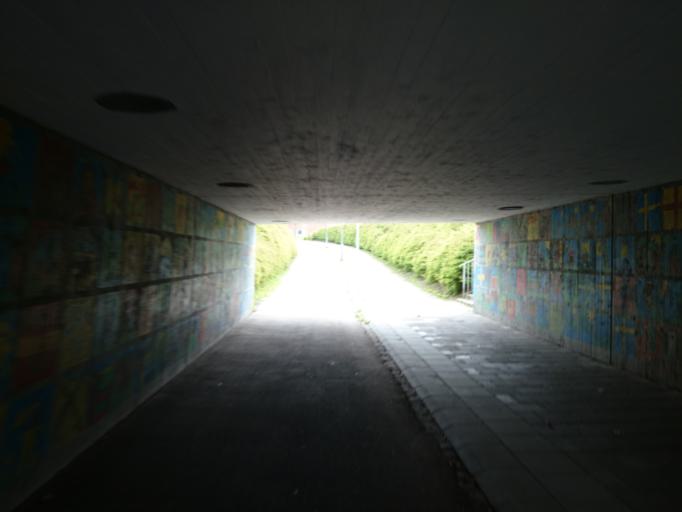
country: SE
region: Skane
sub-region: Burlovs Kommun
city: Arloev
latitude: 55.5821
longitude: 13.0660
